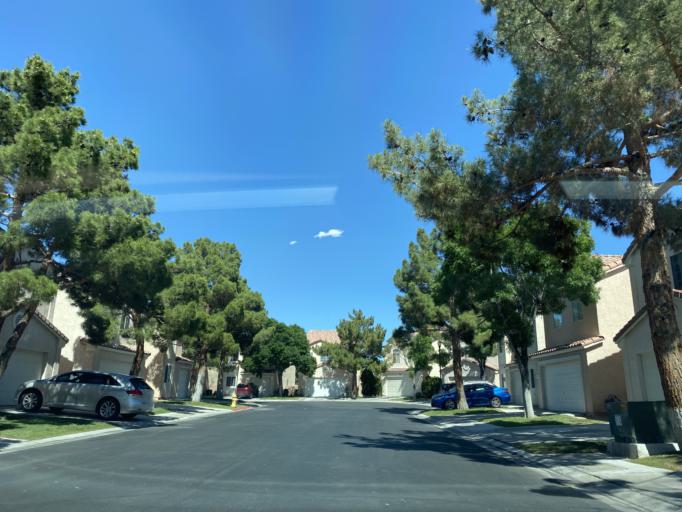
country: US
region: Nevada
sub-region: Clark County
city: Spring Valley
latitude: 36.0915
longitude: -115.2177
